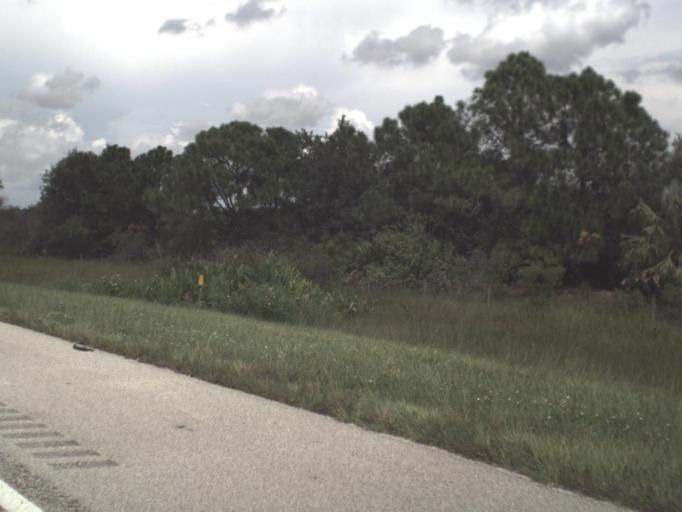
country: US
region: Florida
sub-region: Lee County
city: Suncoast Estates
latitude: 26.7896
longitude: -81.9030
